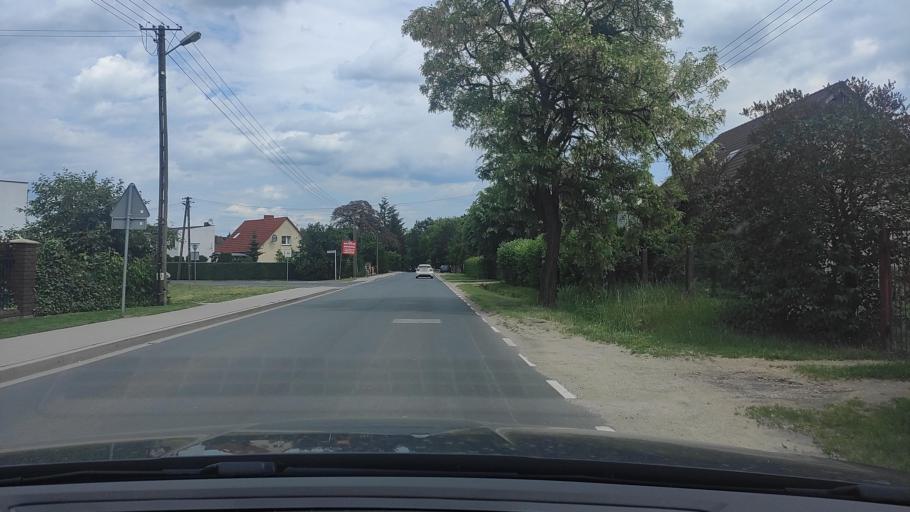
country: PL
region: Greater Poland Voivodeship
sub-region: Powiat poznanski
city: Kostrzyn
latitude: 52.4697
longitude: 17.1765
